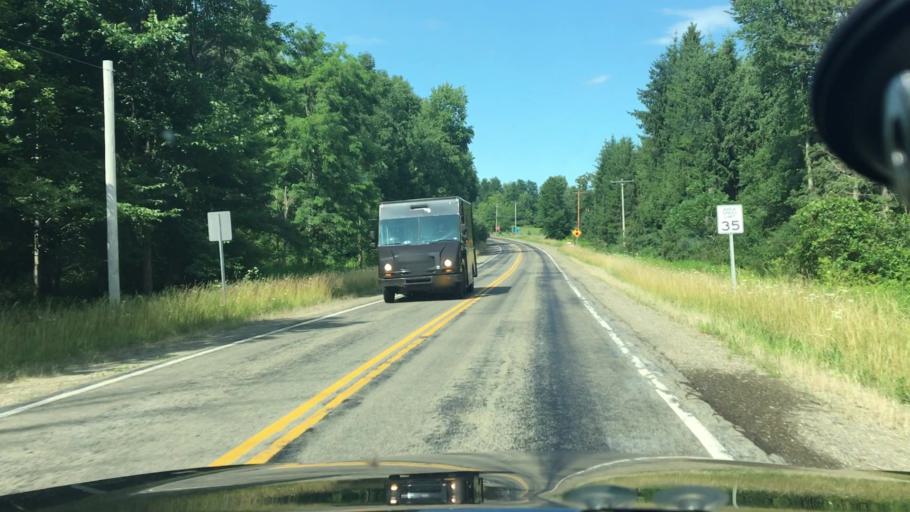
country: US
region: New York
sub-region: Chautauqua County
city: Lakewood
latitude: 42.2568
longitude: -79.3501
